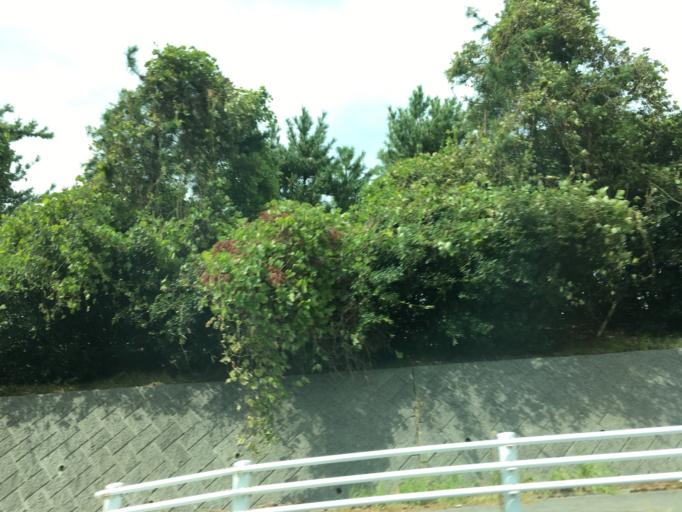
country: JP
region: Hyogo
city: Nishinomiya-hama
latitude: 34.7189
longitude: 135.3217
